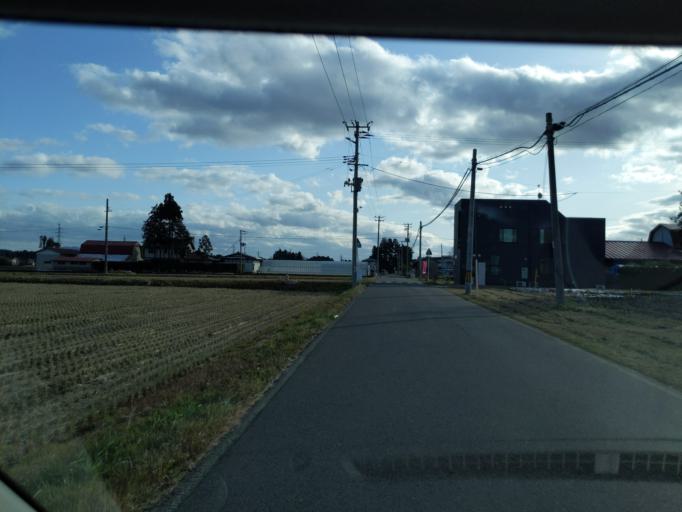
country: JP
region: Iwate
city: Mizusawa
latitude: 39.1379
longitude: 141.0798
